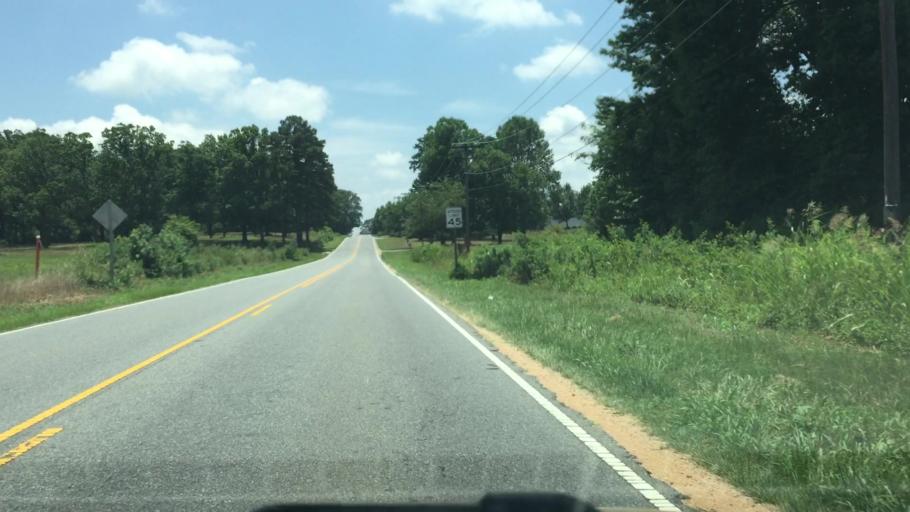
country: US
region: North Carolina
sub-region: Cabarrus County
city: Harrisburg
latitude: 35.4192
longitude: -80.7092
